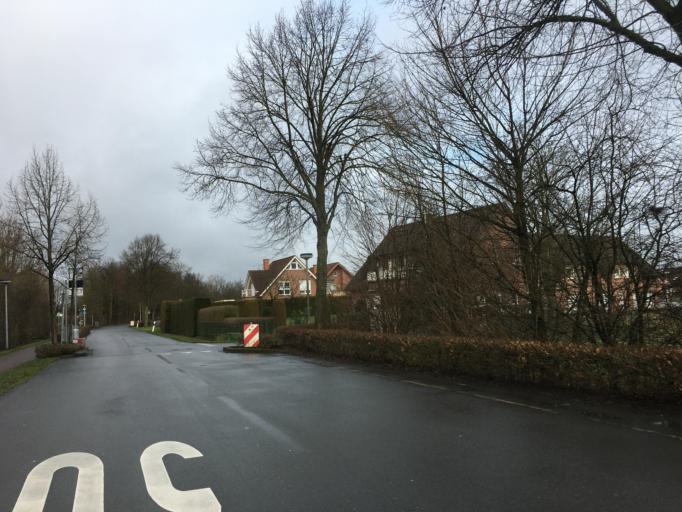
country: DE
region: North Rhine-Westphalia
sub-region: Regierungsbezirk Munster
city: Senden
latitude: 51.9191
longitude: 7.4743
